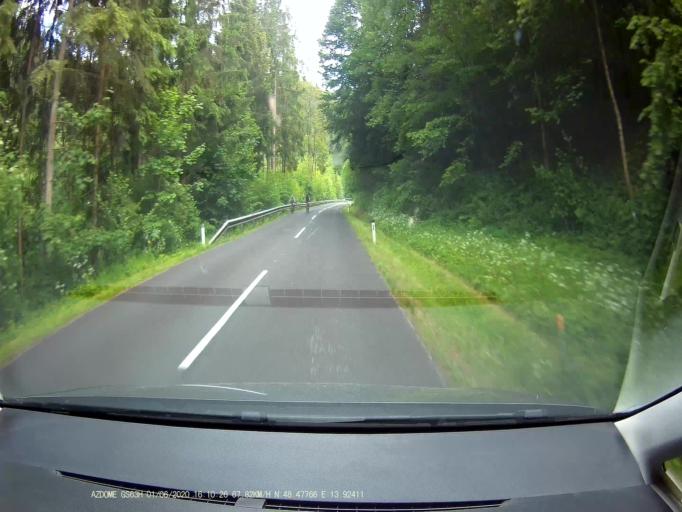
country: AT
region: Upper Austria
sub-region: Politischer Bezirk Rohrbach
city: Atzesberg
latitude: 48.4774
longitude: 13.9244
